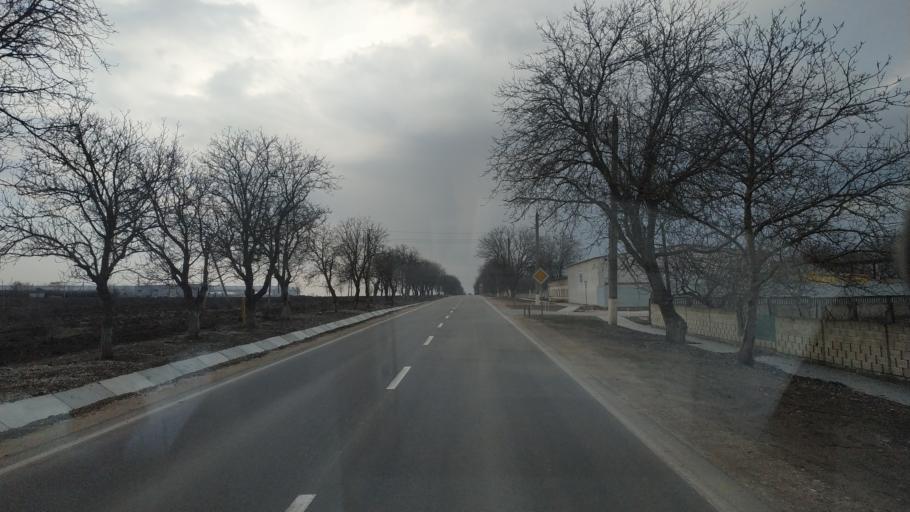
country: MD
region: Telenesti
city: Grigoriopol
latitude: 47.0140
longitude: 29.2890
